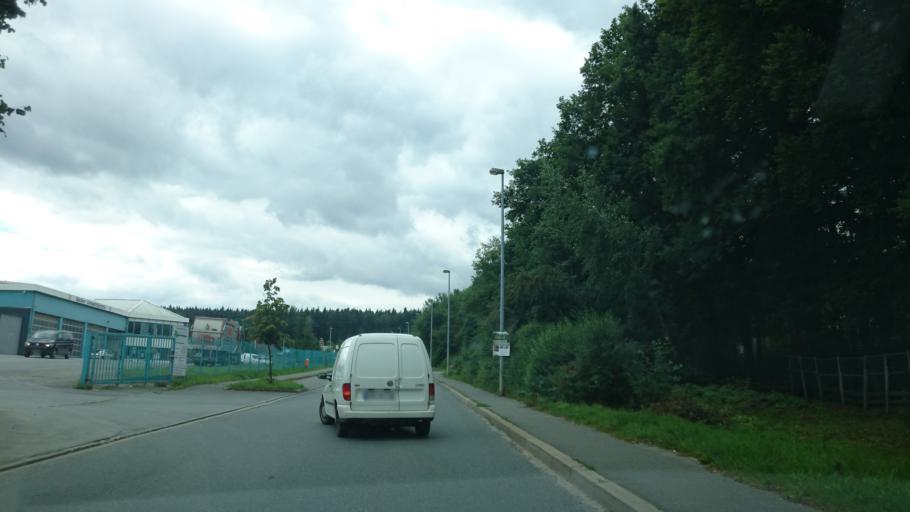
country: DE
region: Thuringia
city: Gorkwitz
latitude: 50.5528
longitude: 11.7869
